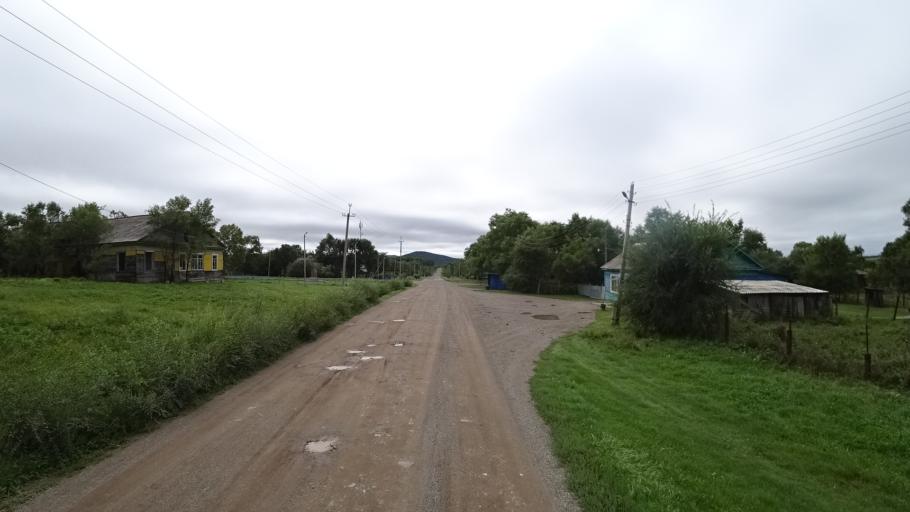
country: RU
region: Primorskiy
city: Lyalichi
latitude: 44.0779
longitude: 132.4754
